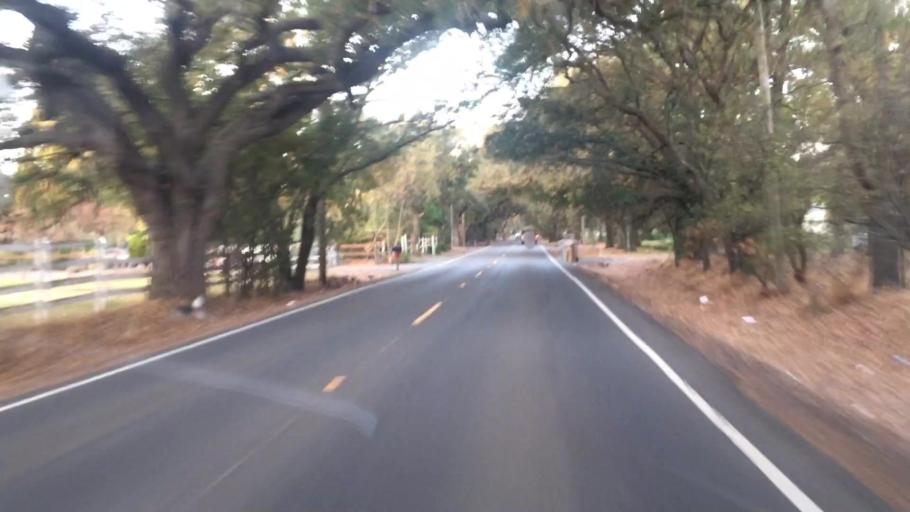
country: US
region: California
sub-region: Sacramento County
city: Wilton
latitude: 38.4382
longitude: -121.3072
